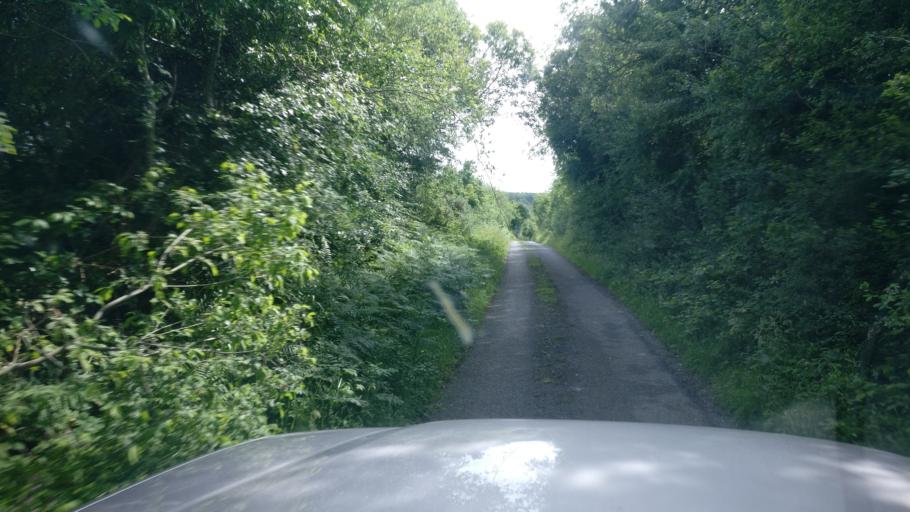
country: IE
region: Connaught
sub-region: County Galway
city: Gort
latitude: 53.0984
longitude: -8.6947
